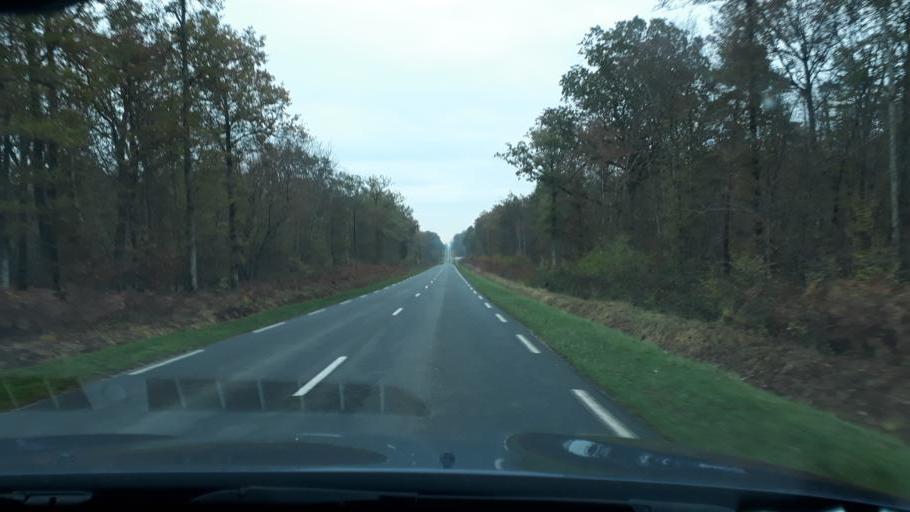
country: FR
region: Centre
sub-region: Departement du Loiret
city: Bouzy-la-Foret
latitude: 47.8273
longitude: 2.4169
